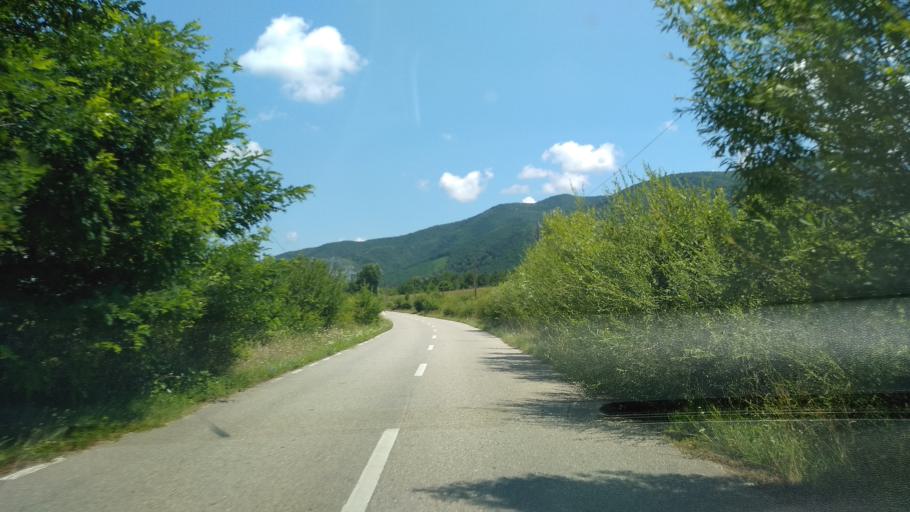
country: RO
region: Hunedoara
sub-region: Comuna Santamaria-Orlea
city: Santamaria-Orlea
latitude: 45.5926
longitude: 23.0026
